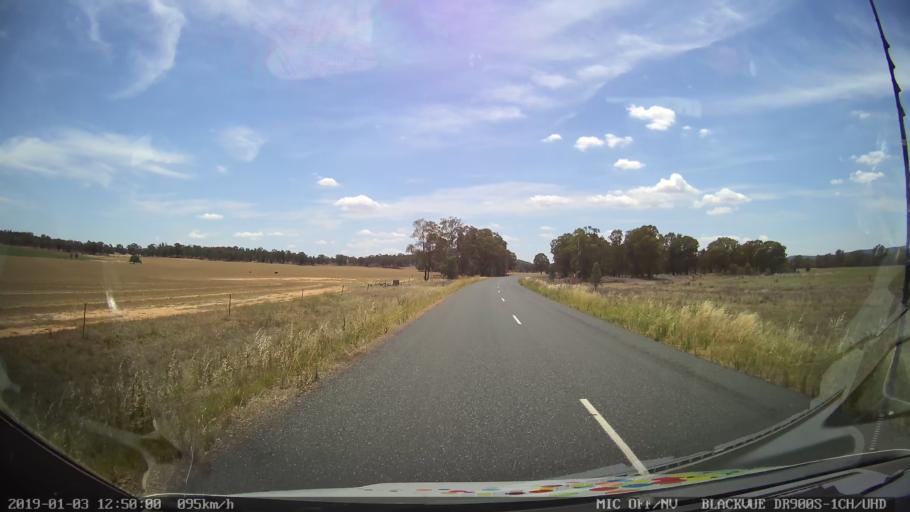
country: AU
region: New South Wales
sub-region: Weddin
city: Grenfell
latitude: -33.6962
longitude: 148.2656
